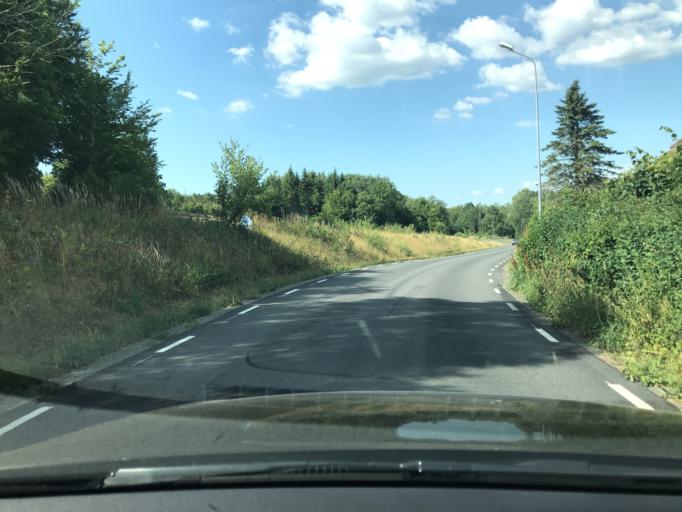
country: SE
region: Skane
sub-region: Hassleholms Kommun
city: Hastveda
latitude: 56.2753
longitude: 13.9127
